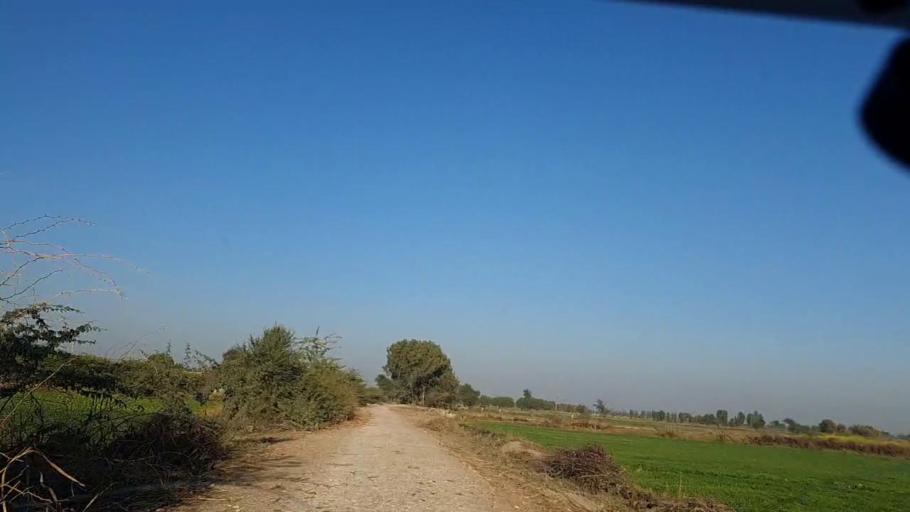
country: PK
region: Sindh
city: Khanpur
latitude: 27.7597
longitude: 69.3369
